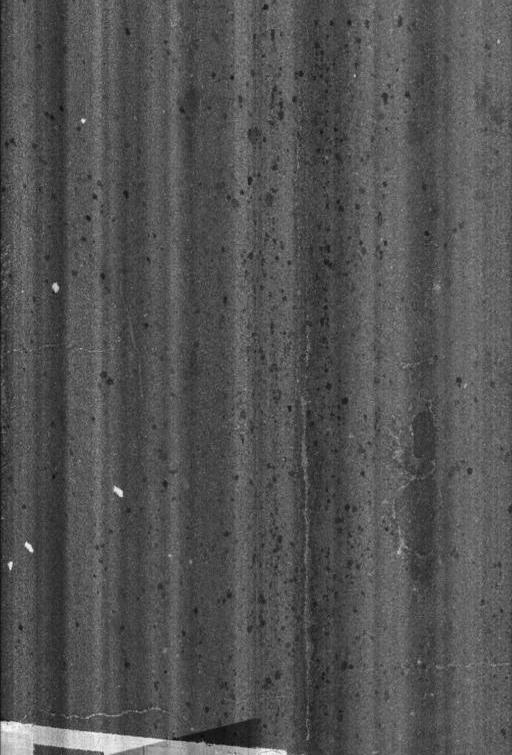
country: US
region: Maryland
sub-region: Prince George's County
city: Glassmanor
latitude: 38.8250
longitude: -76.9997
